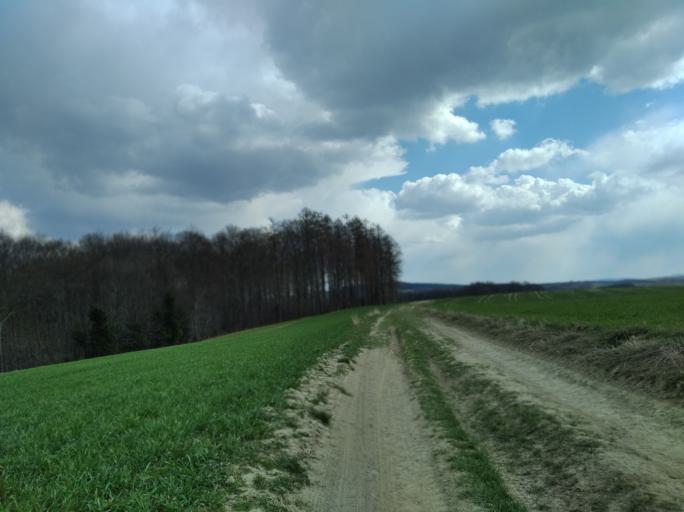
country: PL
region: Subcarpathian Voivodeship
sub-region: Powiat strzyzowski
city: Strzyzow
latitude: 49.9229
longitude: 21.7392
